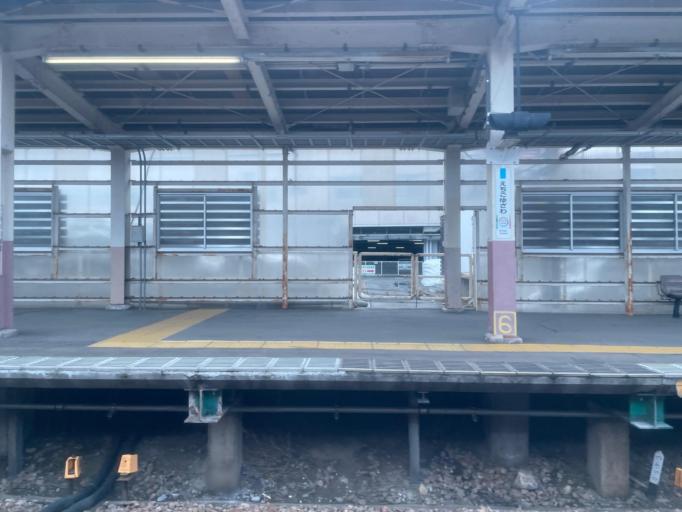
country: JP
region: Niigata
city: Shiozawa
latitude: 36.9354
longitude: 138.8105
